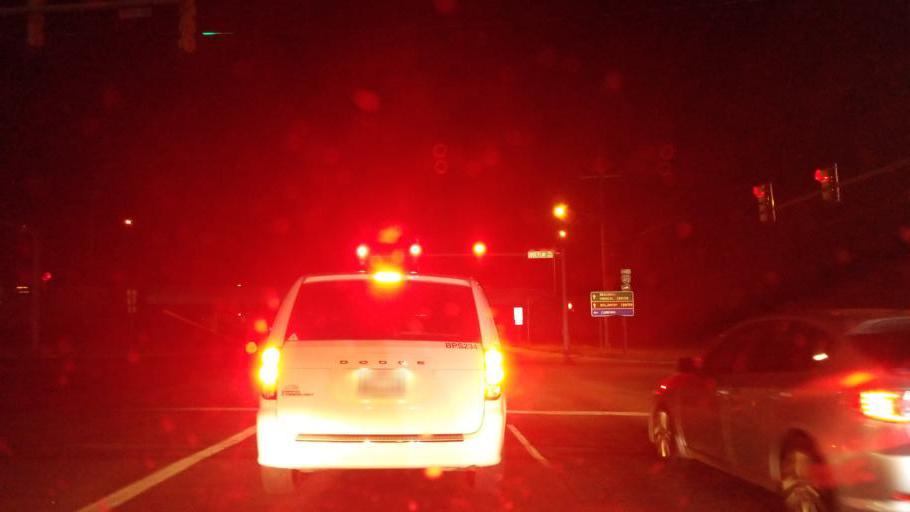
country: US
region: Texas
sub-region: Potter County
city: Amarillo
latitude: 35.1911
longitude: -101.9203
